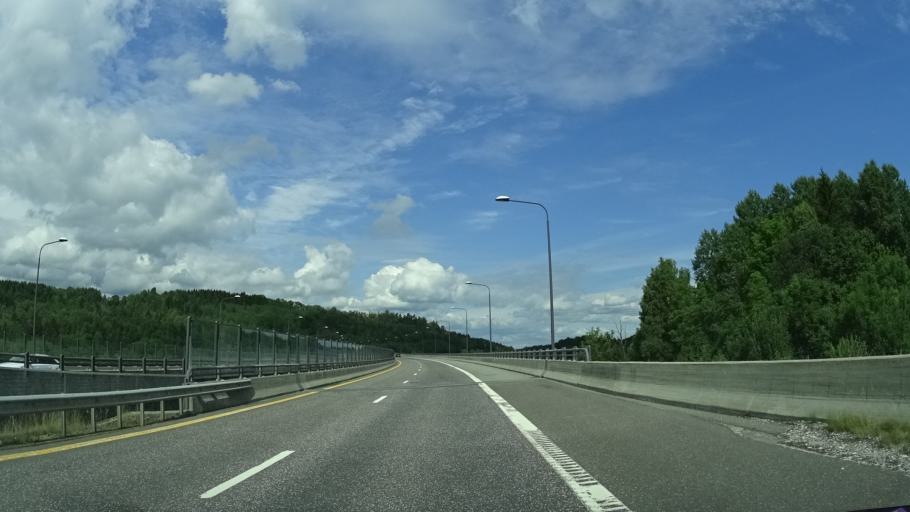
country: NO
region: Vestfold
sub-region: Holmestrand
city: Holmestrand
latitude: 59.4496
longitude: 10.3556
